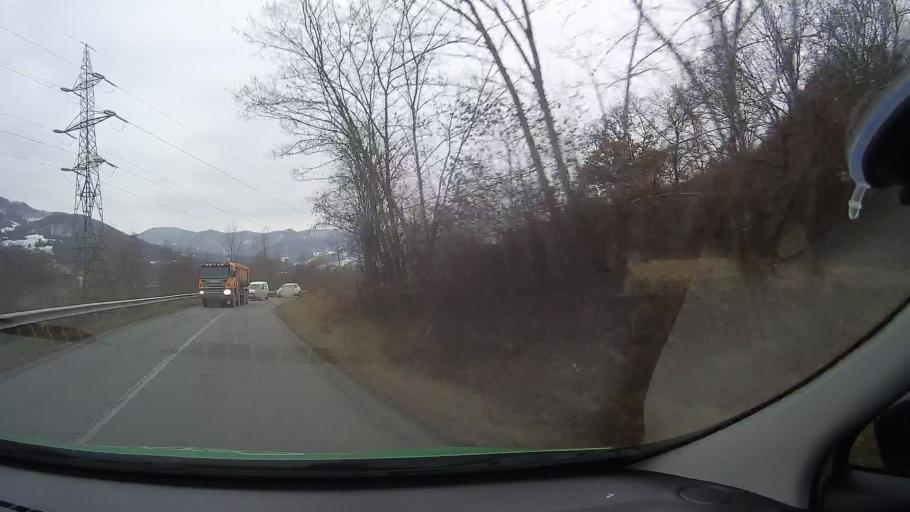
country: RO
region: Alba
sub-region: Comuna Ighiu
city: Ighiel
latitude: 46.1031
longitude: 23.4782
